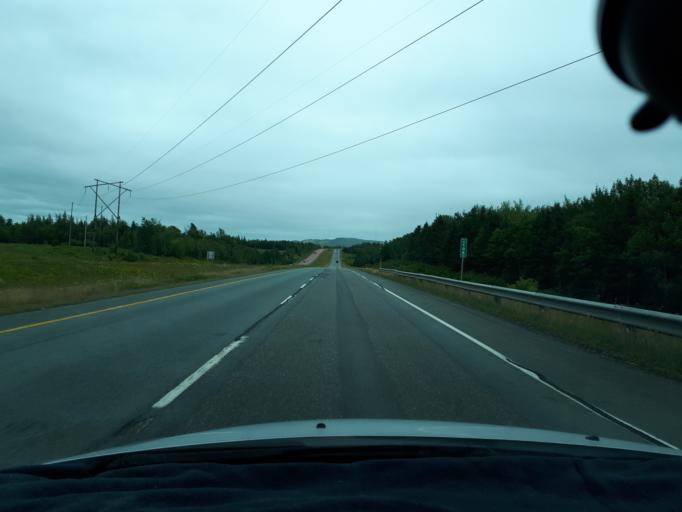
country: CA
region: Nova Scotia
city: Truro
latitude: 45.3958
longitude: -63.3049
